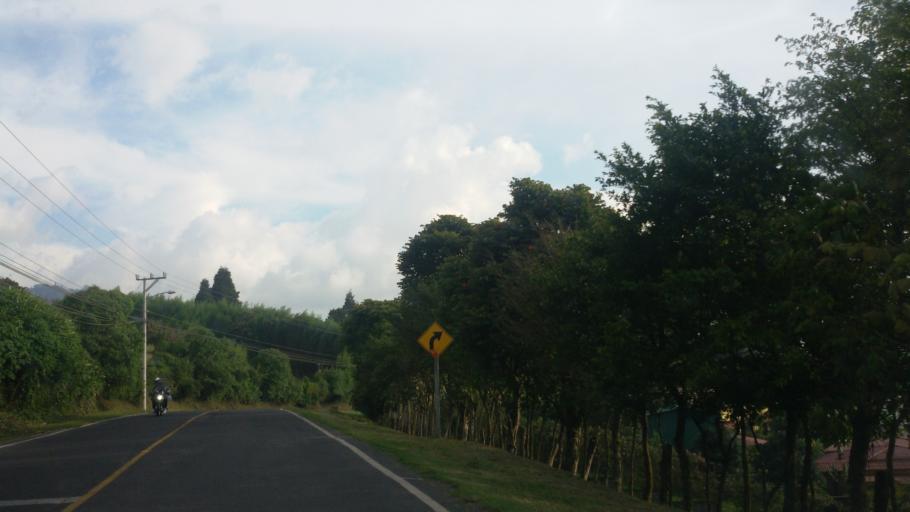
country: CR
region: San Jose
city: Ipis
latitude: 9.9862
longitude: -83.9613
